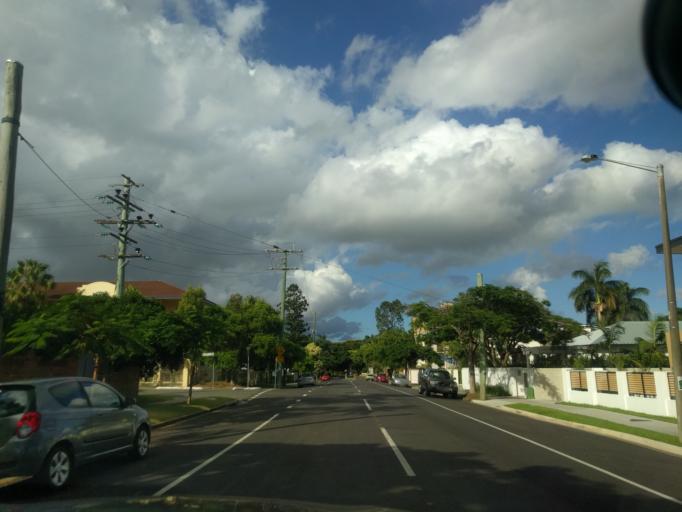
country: AU
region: Queensland
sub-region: Brisbane
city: Balmoral
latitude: -27.4722
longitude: 153.0501
